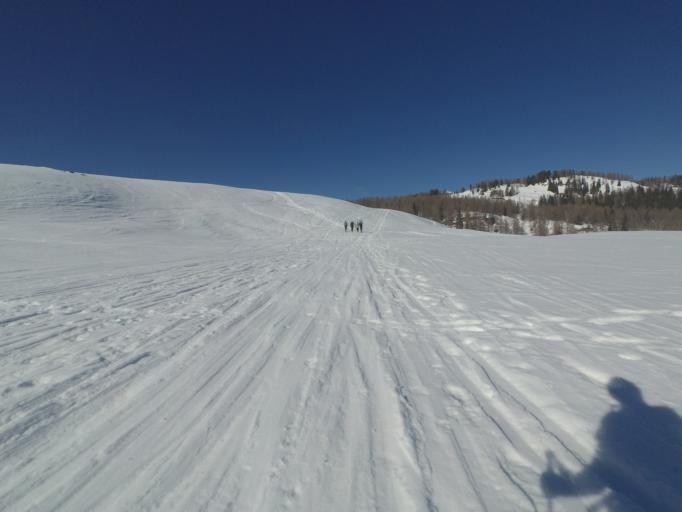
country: AT
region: Upper Austria
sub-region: Politischer Bezirk Gmunden
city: Sankt Wolfgang im Salzkammergut
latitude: 47.6542
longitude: 13.3990
